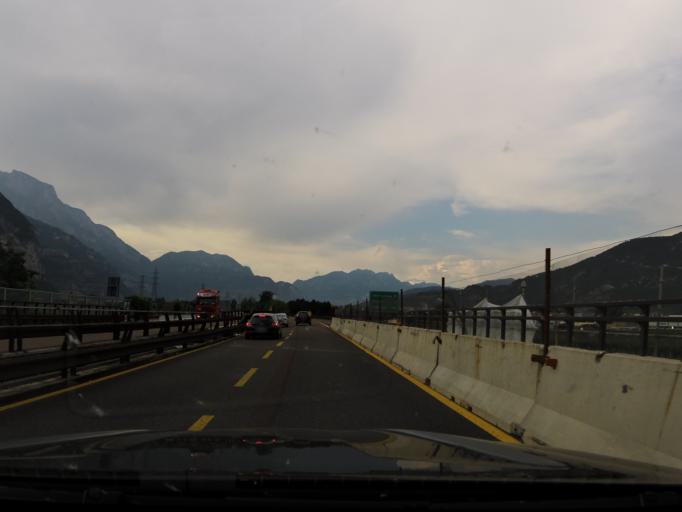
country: IT
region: Trentino-Alto Adige
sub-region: Provincia di Trento
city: Trento
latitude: 46.0842
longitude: 11.1051
